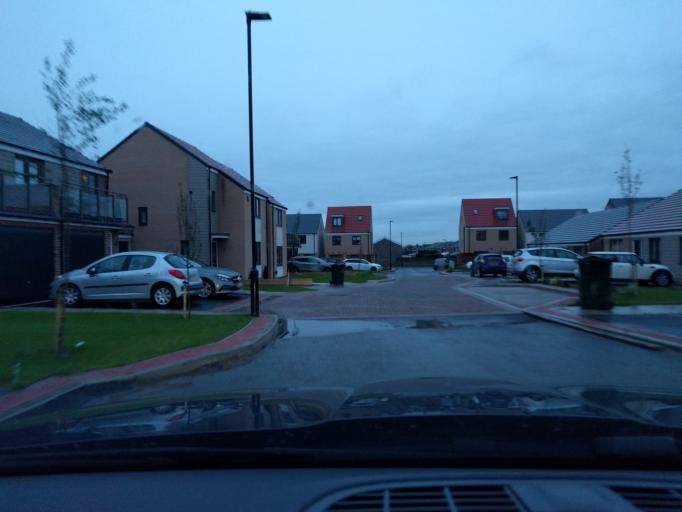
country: GB
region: England
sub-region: Borough of North Tyneside
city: Wallsend
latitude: 55.0109
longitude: -1.5462
